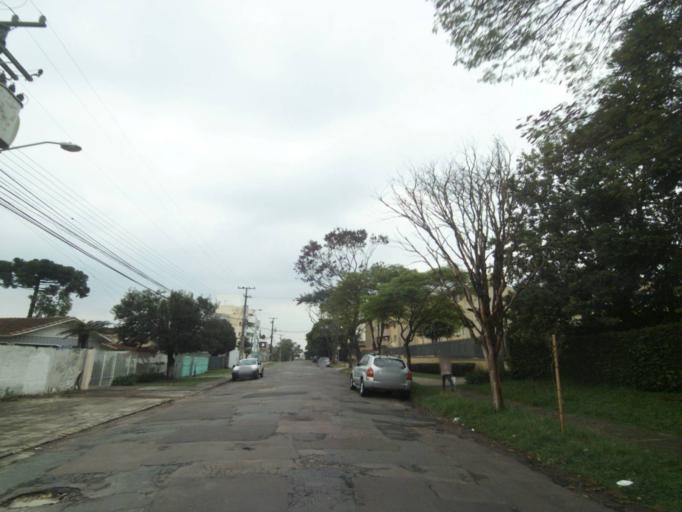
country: BR
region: Parana
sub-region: Curitiba
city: Curitiba
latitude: -25.4760
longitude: -49.3082
